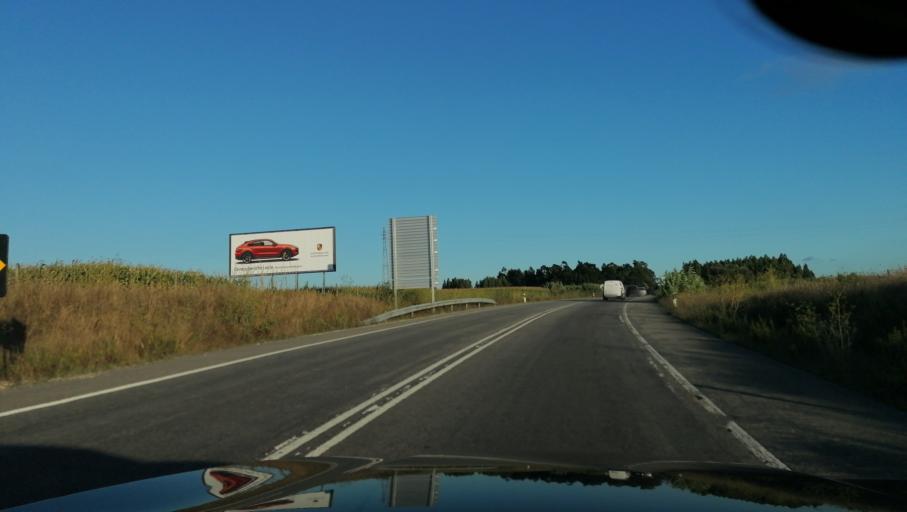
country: PT
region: Aveiro
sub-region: Aveiro
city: Aradas
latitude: 40.6097
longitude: -8.6252
